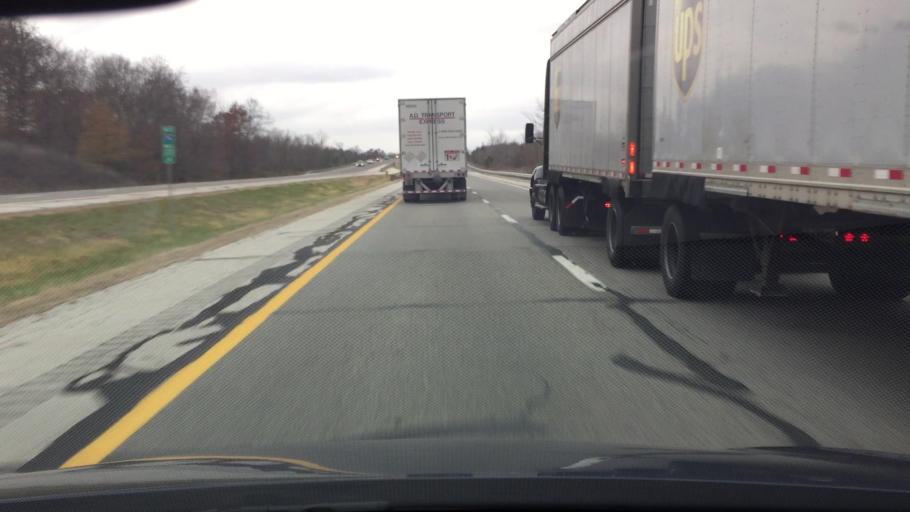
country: US
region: Ohio
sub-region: Mahoning County
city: Austintown
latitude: 41.0625
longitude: -80.7830
